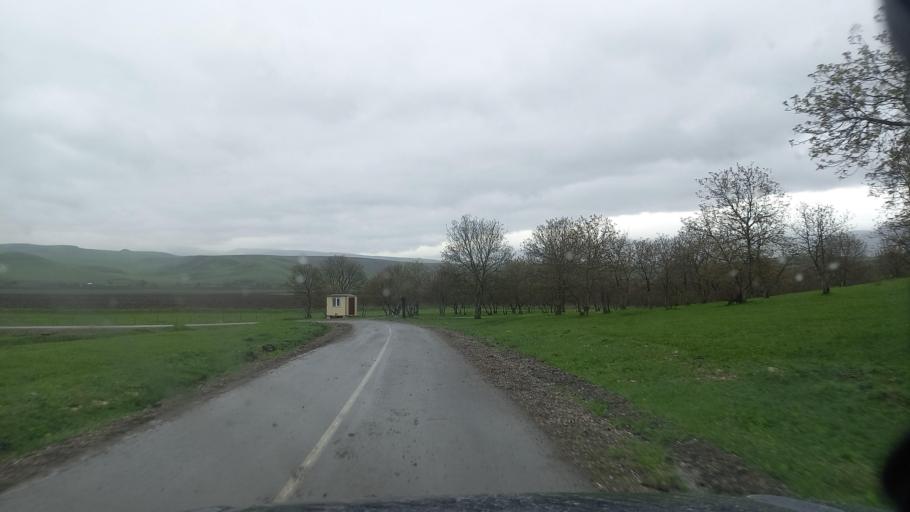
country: RU
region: Kabardino-Balkariya
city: Kamennomostskoye
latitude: 43.7057
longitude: 43.0712
